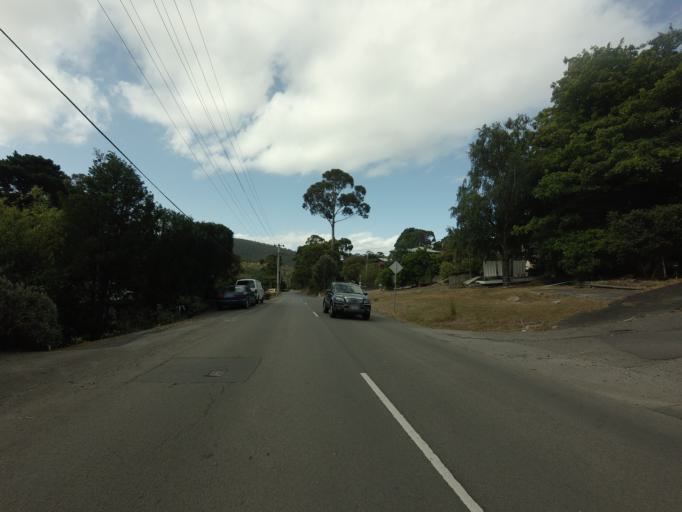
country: AU
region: Tasmania
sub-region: Hobart
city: Dynnyrne
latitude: -42.9012
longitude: 147.2811
